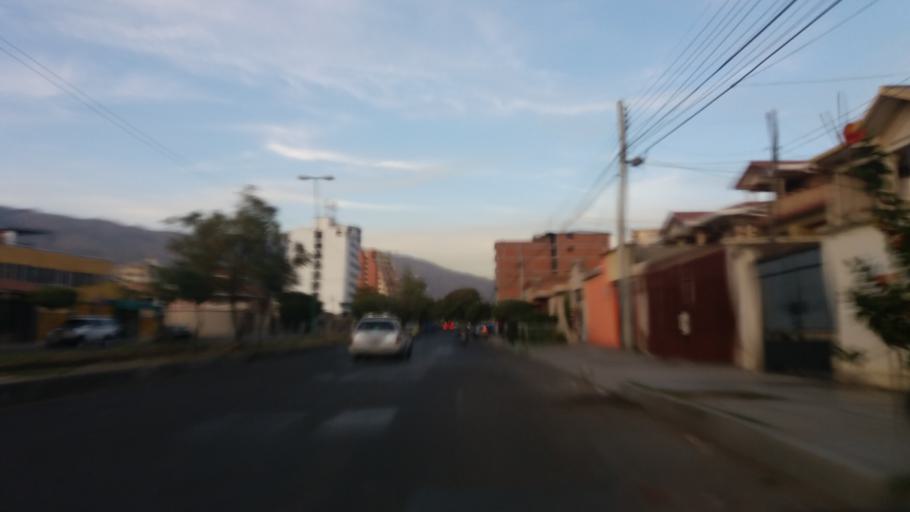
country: BO
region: Cochabamba
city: Cochabamba
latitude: -17.3827
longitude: -66.1787
